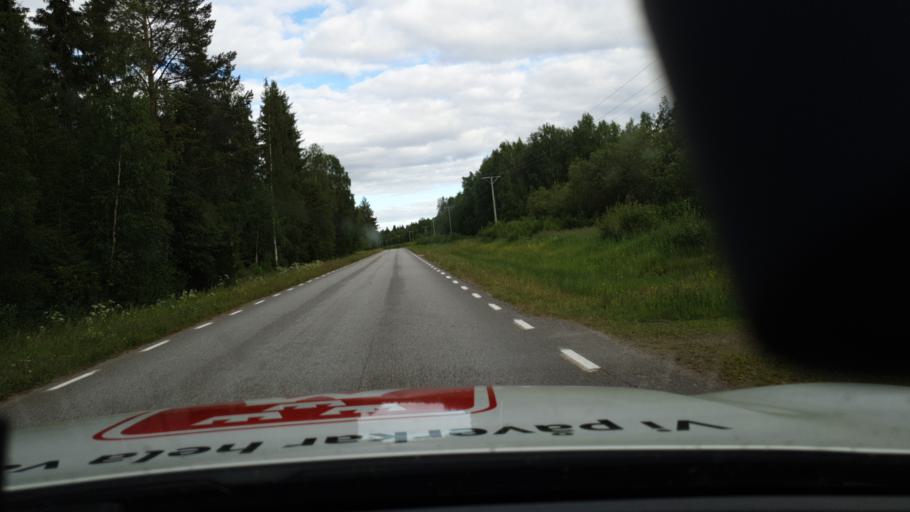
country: SE
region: Norrbotten
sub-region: Kalix Kommun
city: Toere
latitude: 65.8946
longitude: 22.6329
